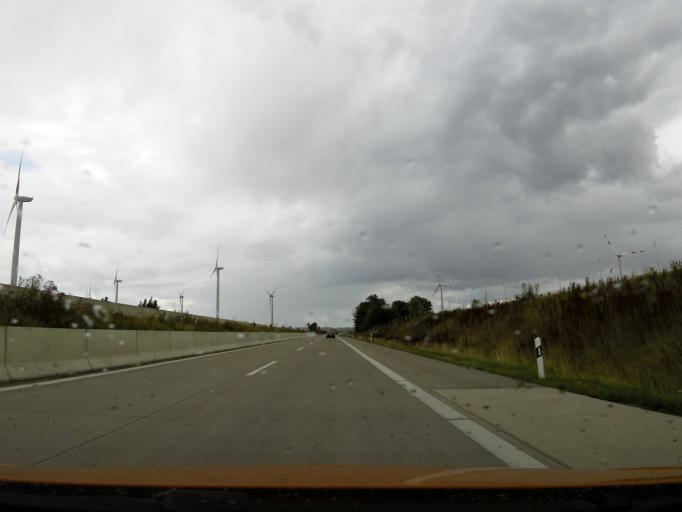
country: DE
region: Brandenburg
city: Gramzow
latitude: 53.2665
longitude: 14.0432
